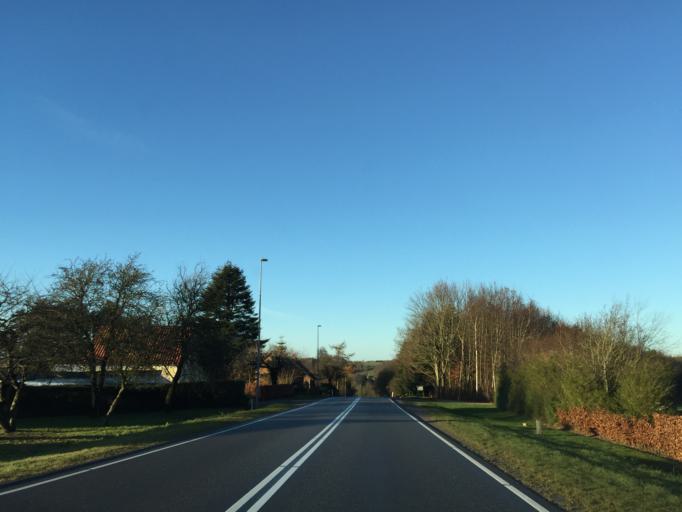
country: DK
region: Central Jutland
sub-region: Skanderborg Kommune
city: Skanderborg
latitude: 56.0502
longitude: 9.9189
